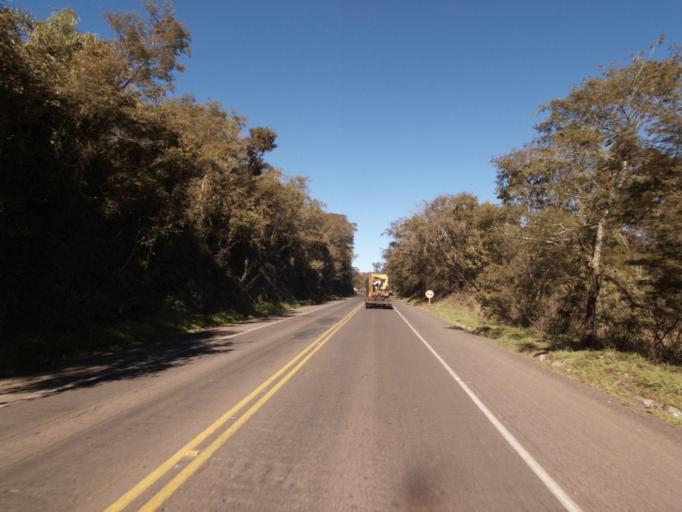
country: BR
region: Santa Catarina
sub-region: Chapeco
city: Chapeco
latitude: -26.9457
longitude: -52.7821
